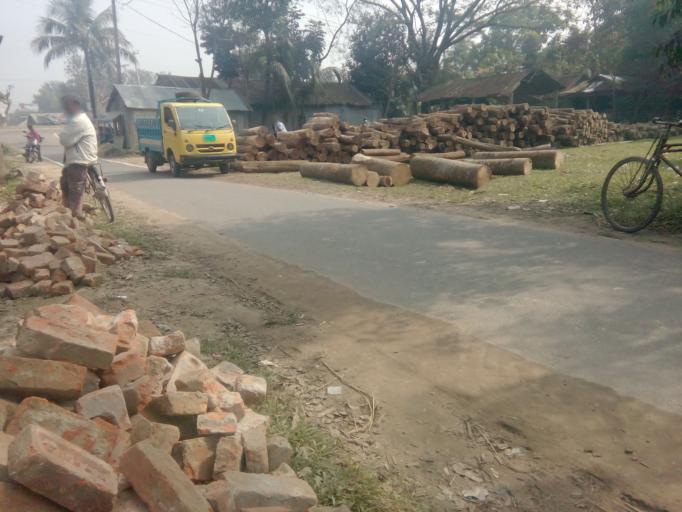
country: IN
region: Tripura
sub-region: West Tripura
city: Sonamura
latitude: 23.3223
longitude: 91.2798
